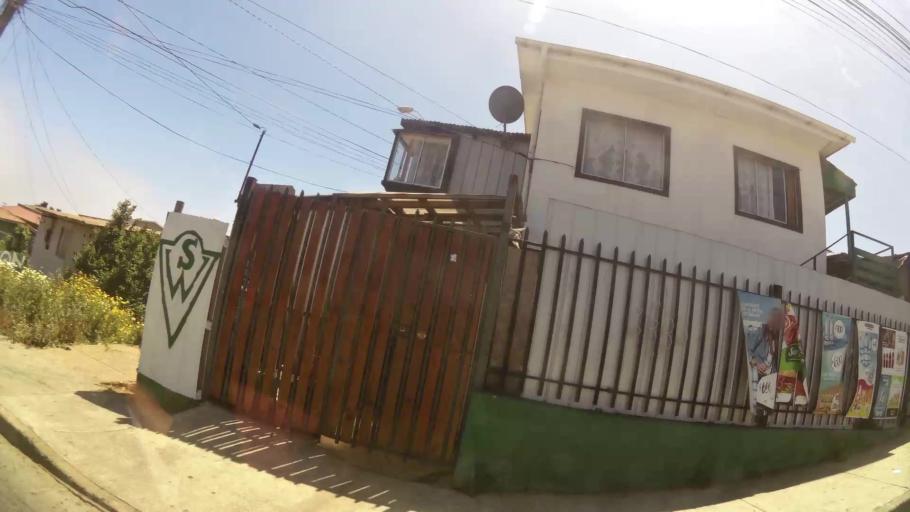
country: CL
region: Valparaiso
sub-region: Provincia de Valparaiso
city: Valparaiso
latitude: -33.0318
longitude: -71.6497
